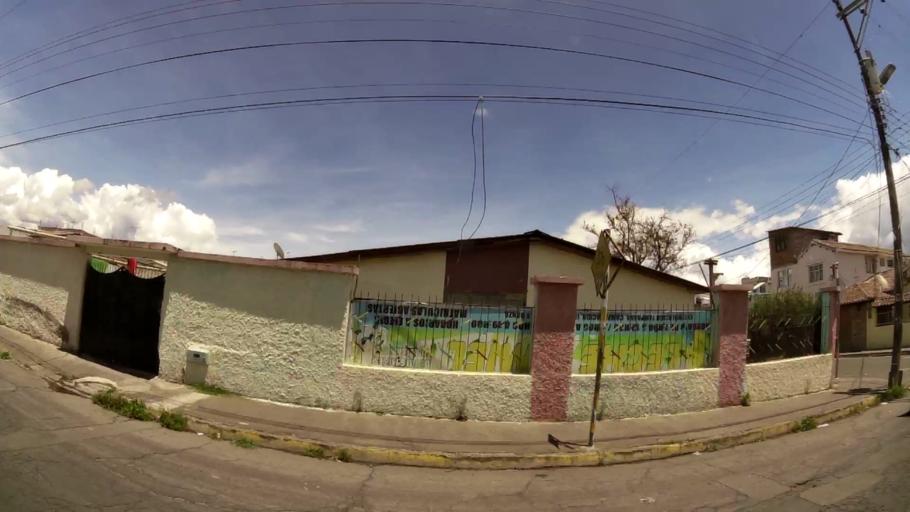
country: EC
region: Chimborazo
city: Riobamba
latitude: -1.6730
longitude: -78.6383
